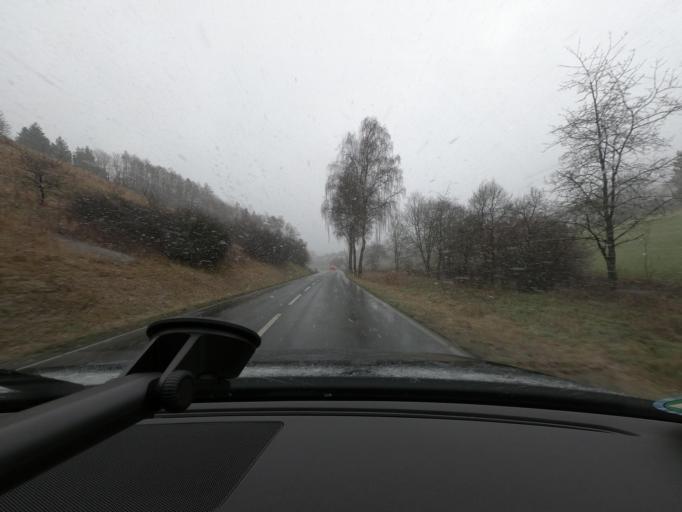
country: DE
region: North Rhine-Westphalia
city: Marsberg
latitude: 51.5007
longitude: 8.9058
